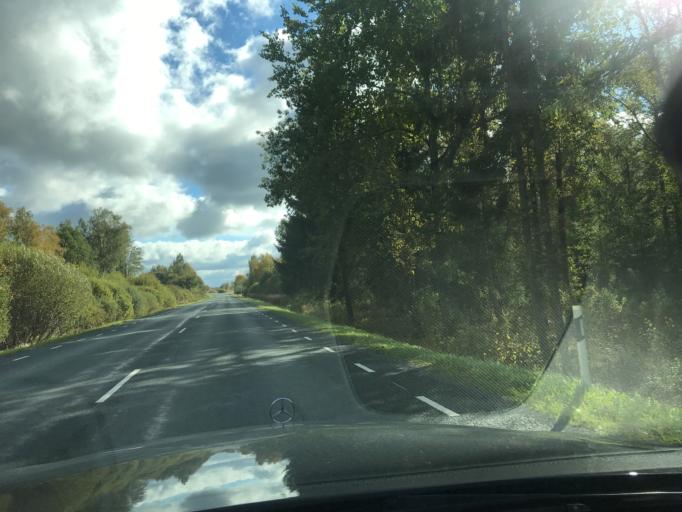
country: EE
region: Vorumaa
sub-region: Antsla vald
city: Vana-Antsla
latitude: 57.9142
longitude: 26.3892
